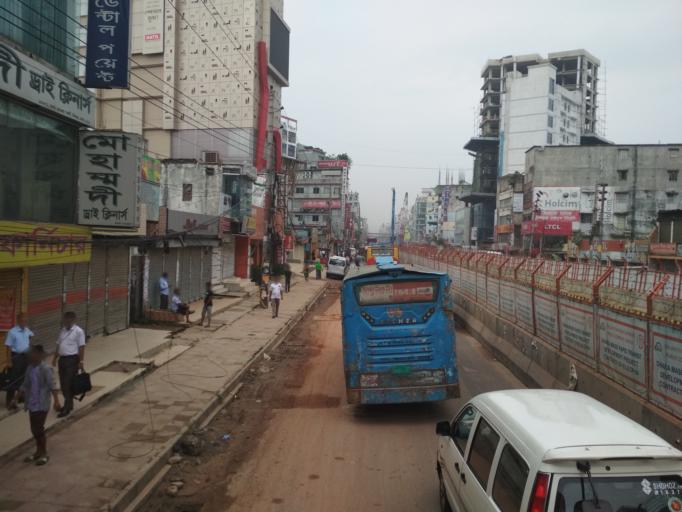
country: BD
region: Dhaka
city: Azimpur
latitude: 23.8014
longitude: 90.3712
